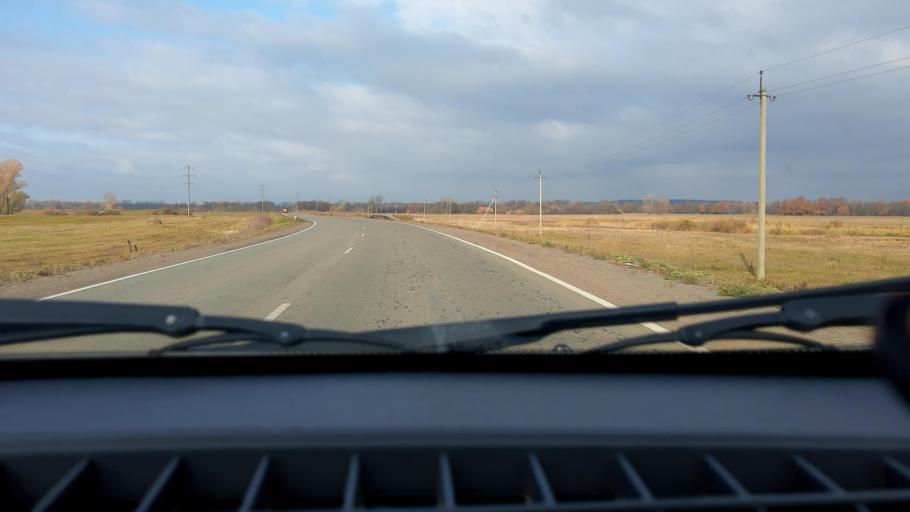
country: RU
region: Bashkortostan
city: Kabakovo
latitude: 54.5589
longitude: 56.0092
